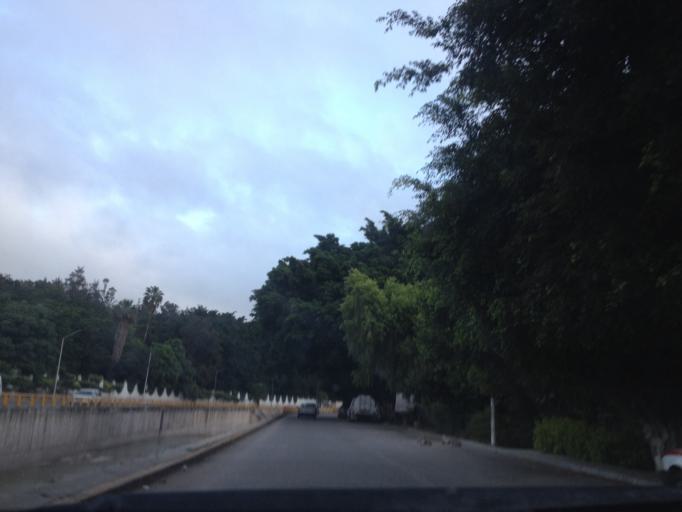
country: MX
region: Guerrero
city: Chilpancingo de los Bravos
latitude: 17.5453
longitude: -99.5018
